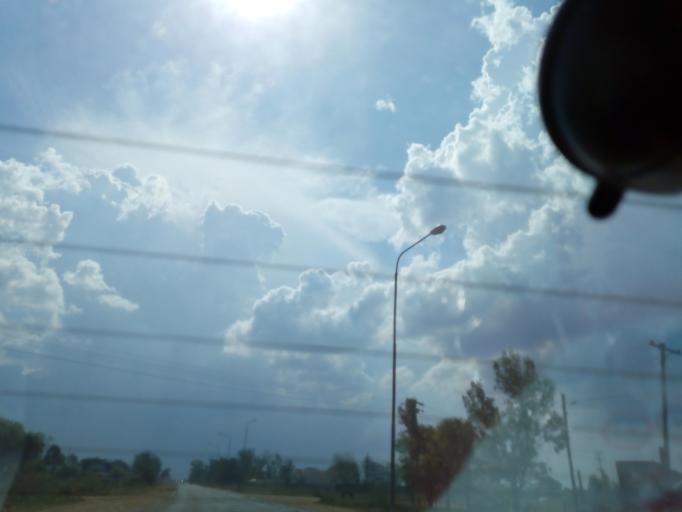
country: AR
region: Corrientes
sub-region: Departamento de Paso de los Libres
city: Paso de los Libres
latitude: -29.7218
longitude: -57.1201
